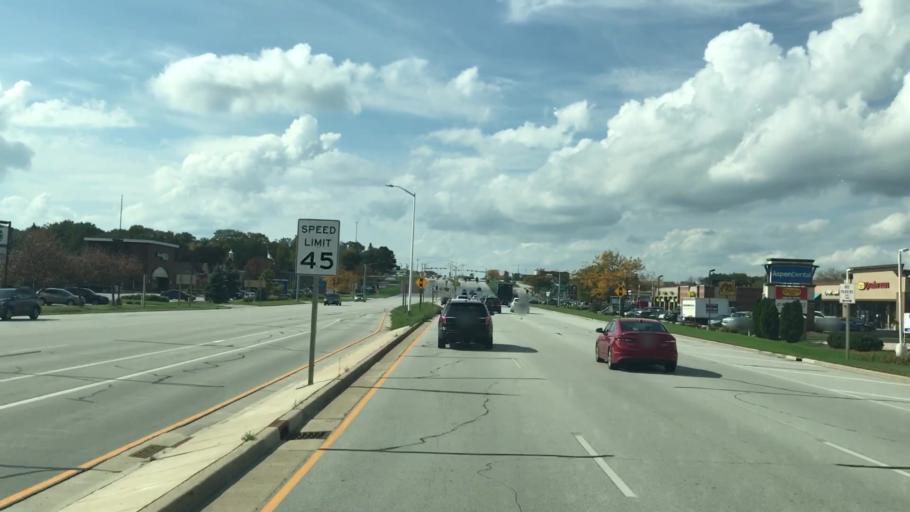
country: US
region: Wisconsin
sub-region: Waukesha County
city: Waukesha
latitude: 43.0316
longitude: -88.1786
